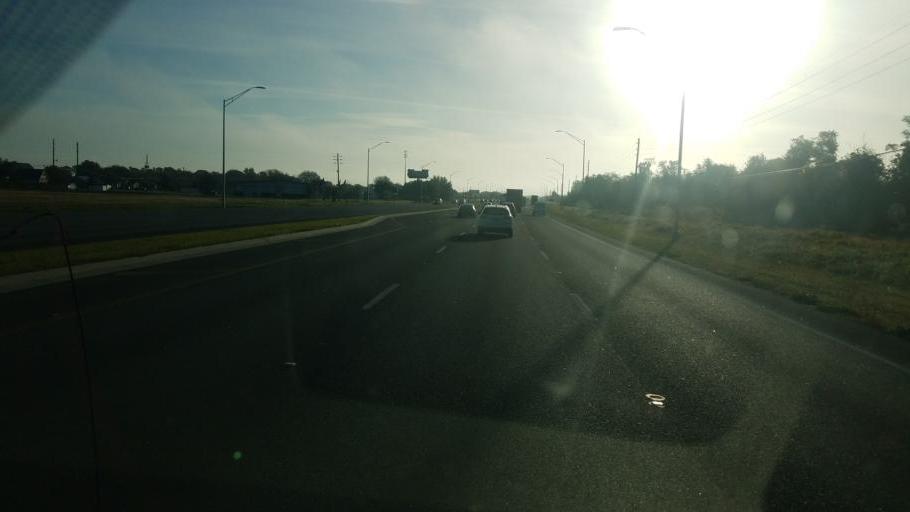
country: US
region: Florida
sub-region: Osceola County
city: Saint Cloud
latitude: 28.2457
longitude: -81.2334
